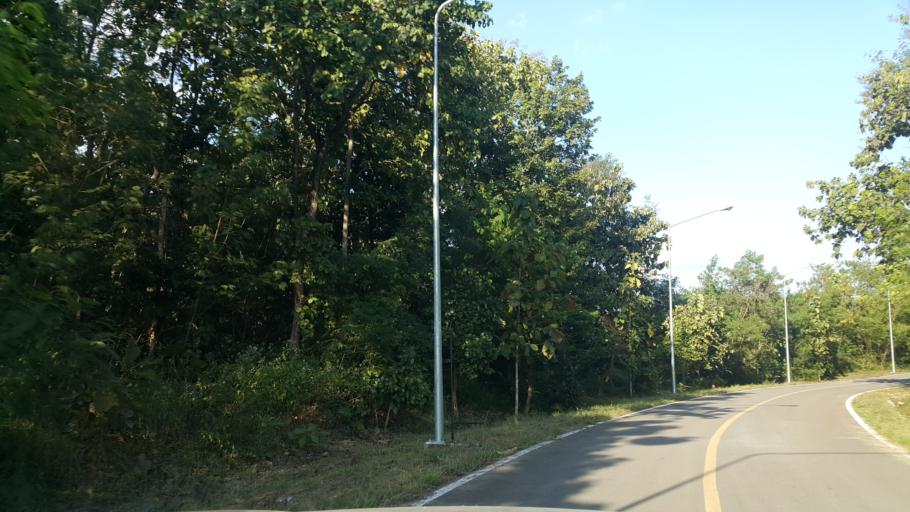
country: TH
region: Lamphun
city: Mae Tha
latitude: 18.5117
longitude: 99.1115
